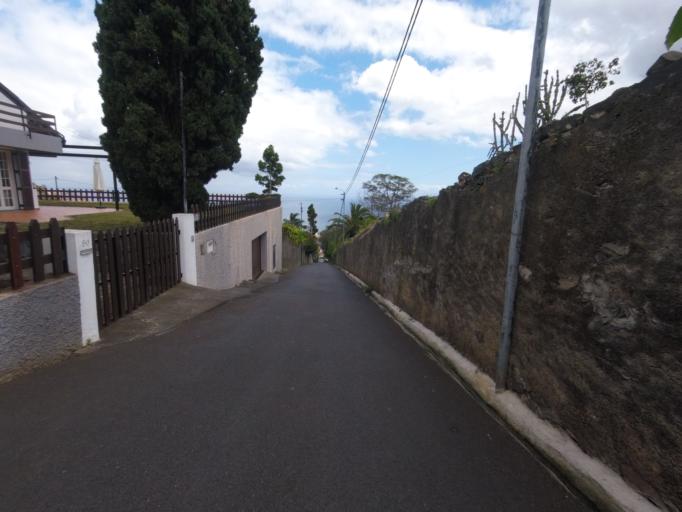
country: PT
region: Madeira
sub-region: Funchal
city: Nossa Senhora do Monte
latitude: 32.6663
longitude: -16.9175
